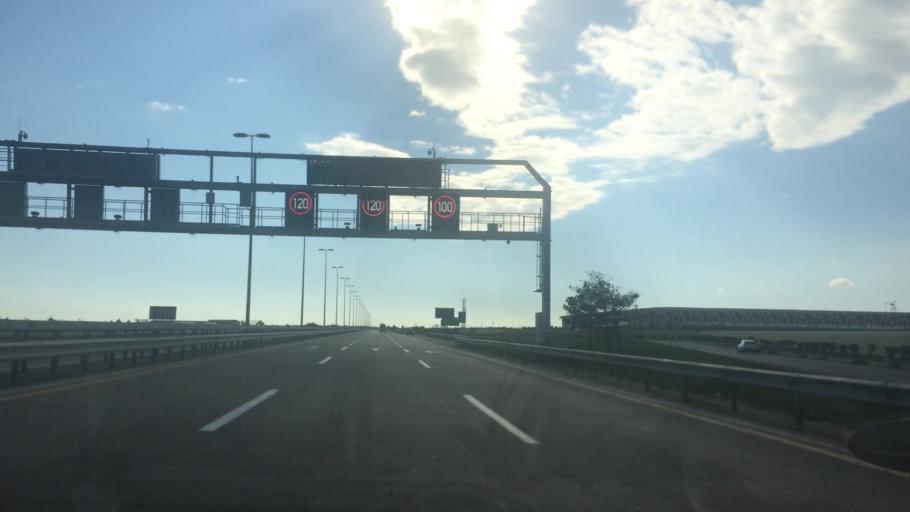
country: AZ
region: Baki
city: Hovsan
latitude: 40.3875
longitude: 50.0674
